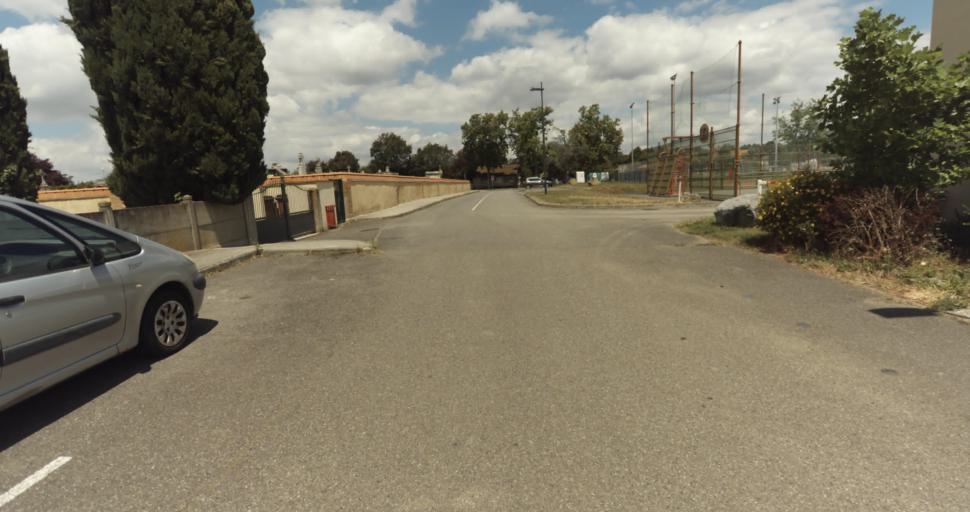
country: FR
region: Midi-Pyrenees
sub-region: Departement de la Haute-Garonne
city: Fontenilles
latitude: 43.5517
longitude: 1.1869
